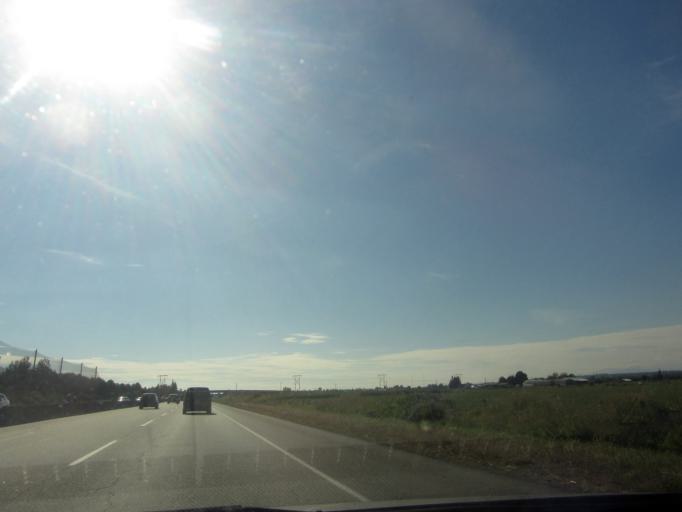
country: CA
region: British Columbia
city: Ladner
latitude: 49.1773
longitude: -123.0382
